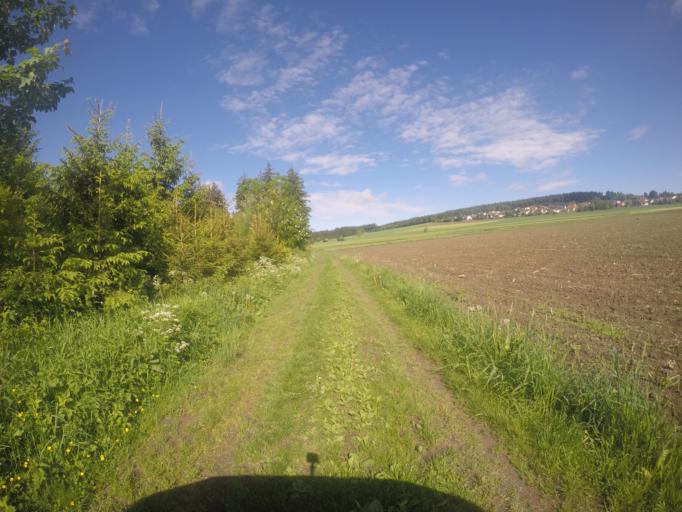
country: DE
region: Bavaria
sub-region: Upper Franconia
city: Schonwald
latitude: 50.1931
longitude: 12.0819
